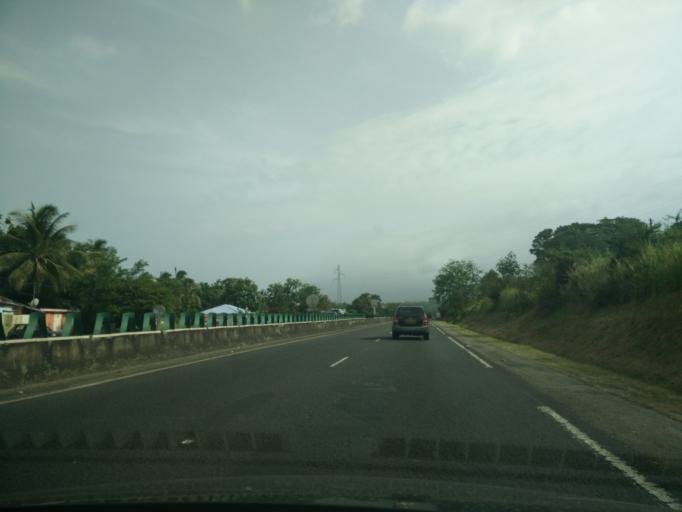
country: GP
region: Guadeloupe
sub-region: Guadeloupe
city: Petit-Bourg
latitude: 16.2112
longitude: -61.6018
